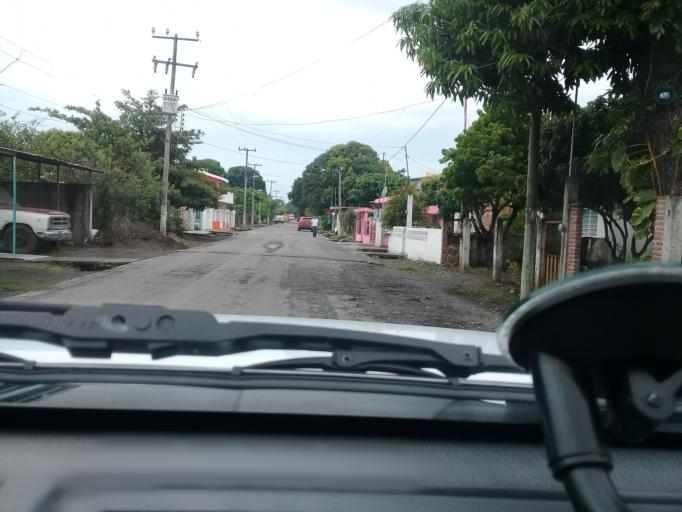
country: MX
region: Veracruz
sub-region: Paso de Ovejas
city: El Hatito
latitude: 19.3175
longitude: -96.3825
